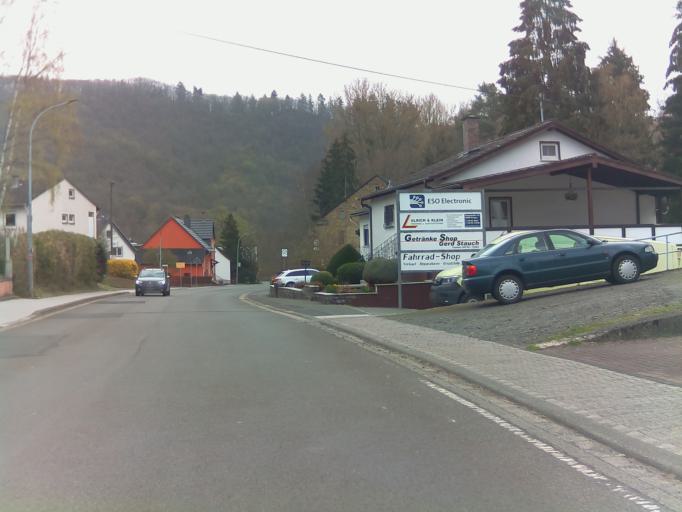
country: DE
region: Rheinland-Pfalz
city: Hahnenbach
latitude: 49.8075
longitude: 7.4202
